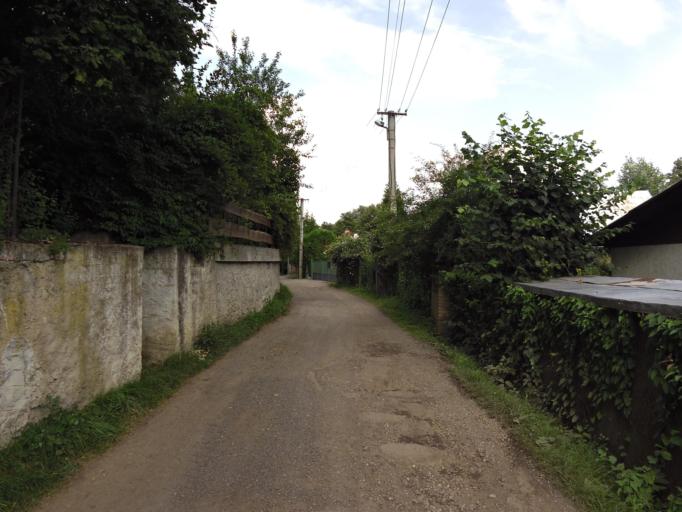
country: CZ
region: Central Bohemia
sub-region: Okres Benesov
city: Cercany
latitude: 49.8743
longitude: 14.7270
